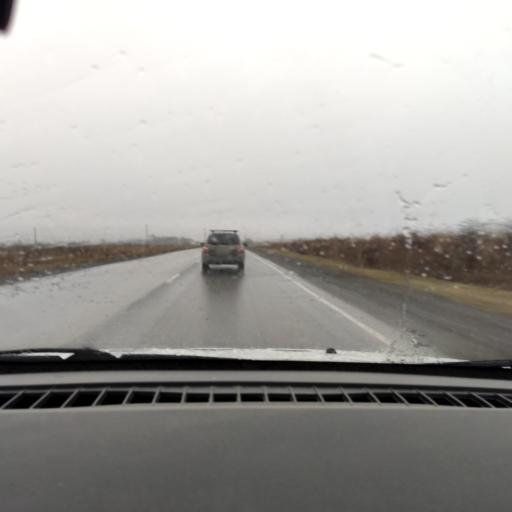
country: RU
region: Perm
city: Froly
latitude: 57.9013
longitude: 56.2168
